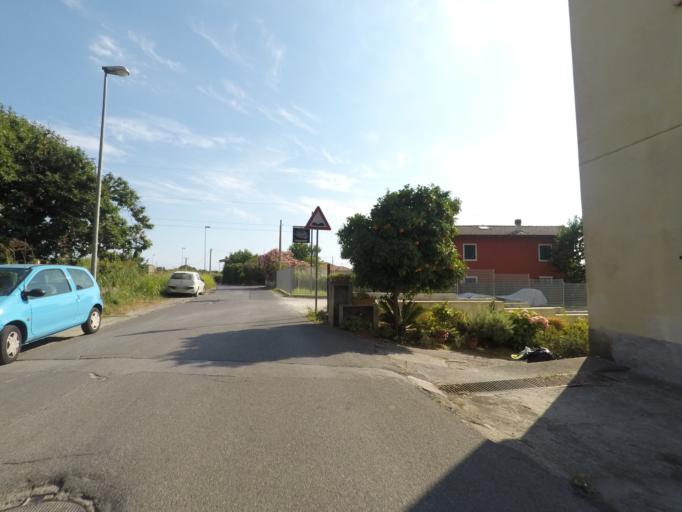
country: IT
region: Tuscany
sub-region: Provincia di Massa-Carrara
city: Capanne-Prato-Cinquale
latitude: 44.0131
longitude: 10.1495
